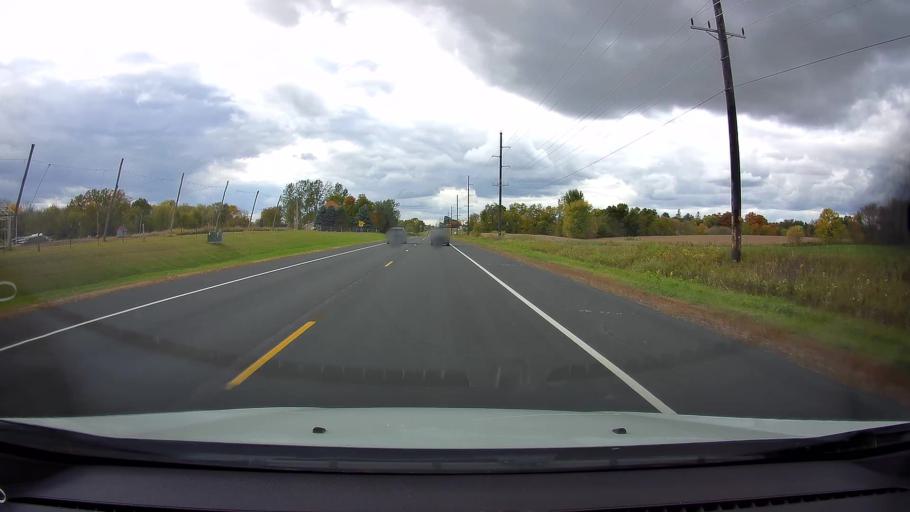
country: US
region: Minnesota
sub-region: Chisago County
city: Shafer
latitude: 45.3972
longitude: -92.7706
